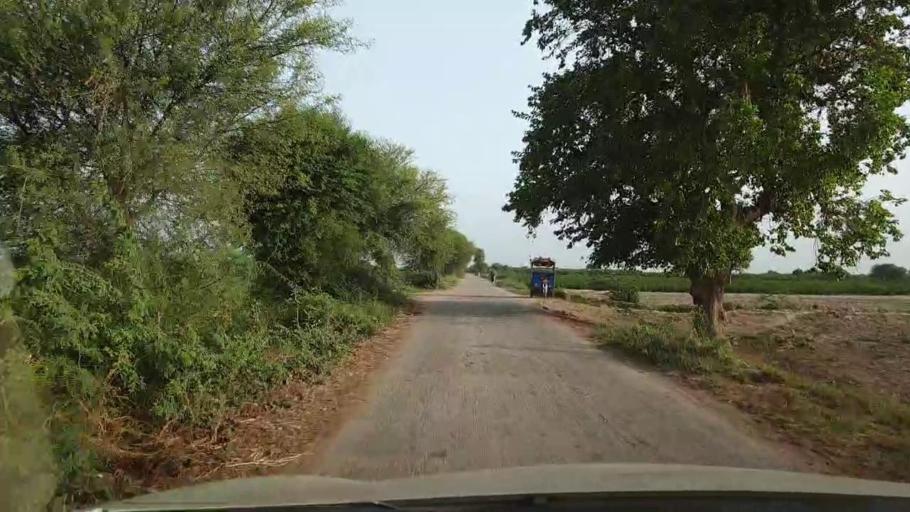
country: PK
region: Sindh
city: Tando Ghulam Ali
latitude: 25.1059
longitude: 68.8848
